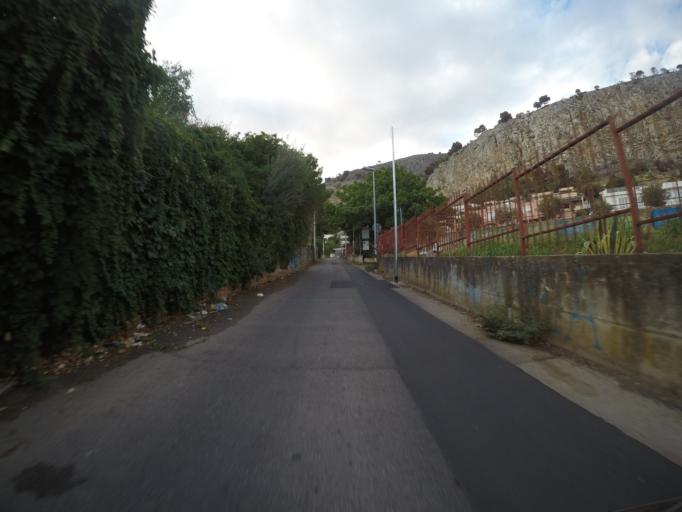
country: IT
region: Sicily
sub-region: Palermo
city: Palermo
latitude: 38.2071
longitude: 13.3222
